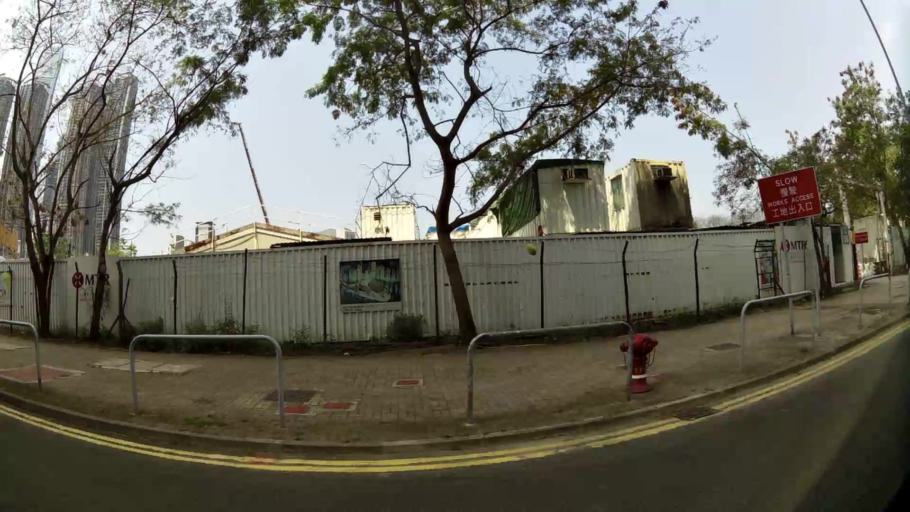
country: HK
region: Kowloon City
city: Kowloon
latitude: 22.3097
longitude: 114.1650
